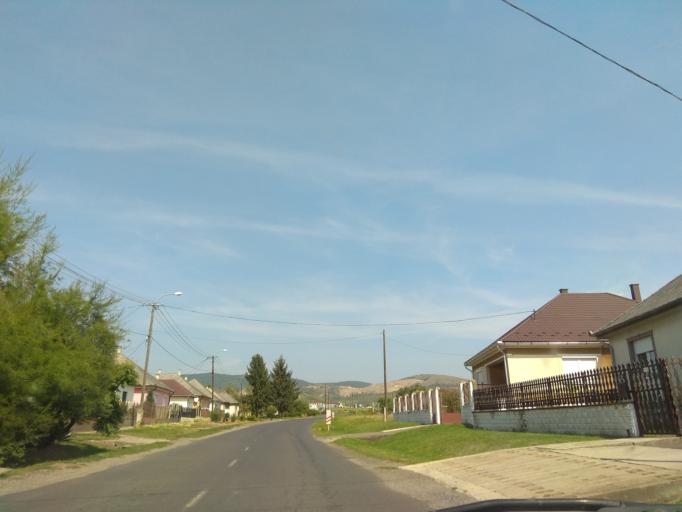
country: HU
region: Borsod-Abauj-Zemplen
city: Tallya
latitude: 48.2215
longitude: 21.2277
